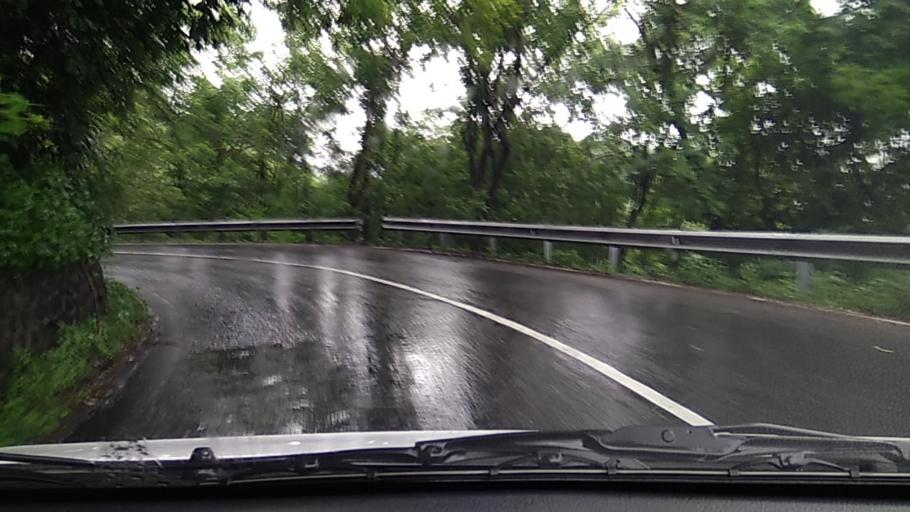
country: ID
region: Bali
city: Banjar Bugbug
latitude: -8.4937
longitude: 115.5869
